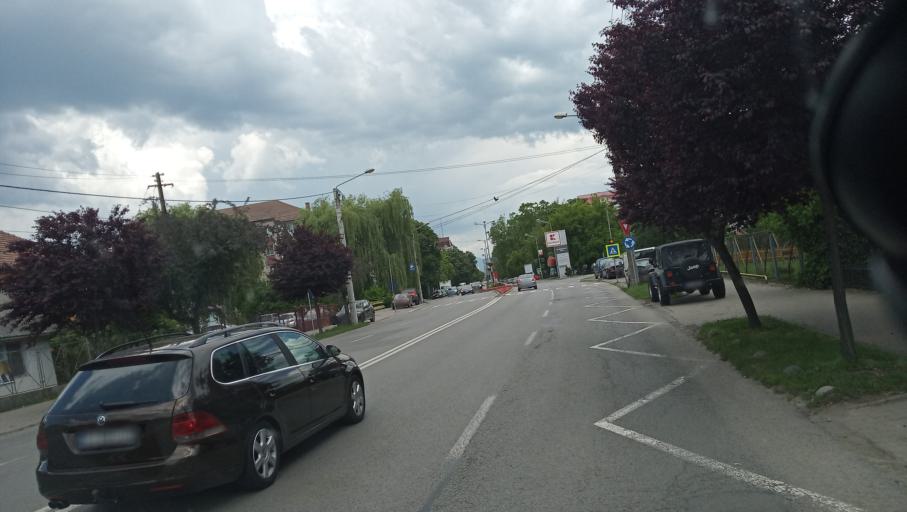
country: RO
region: Bistrita-Nasaud
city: Bistrita
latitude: 47.1235
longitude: 24.4786
